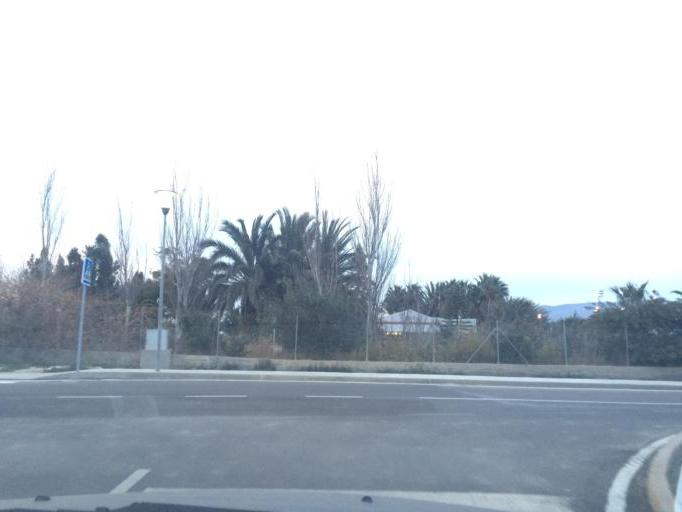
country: ES
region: Andalusia
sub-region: Provincia de Almeria
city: Almeria
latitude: 36.8326
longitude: -2.4018
